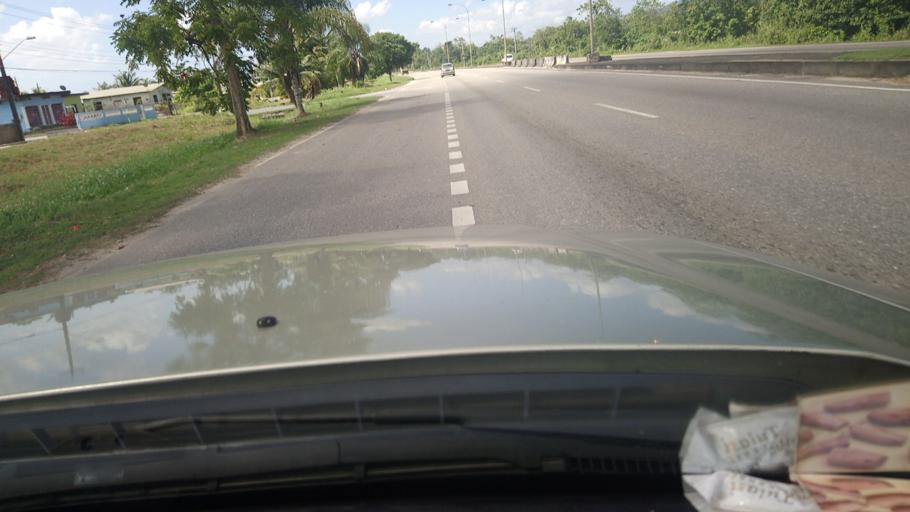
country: TT
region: Borough of Arima
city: Arima
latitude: 10.6294
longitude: -61.2375
